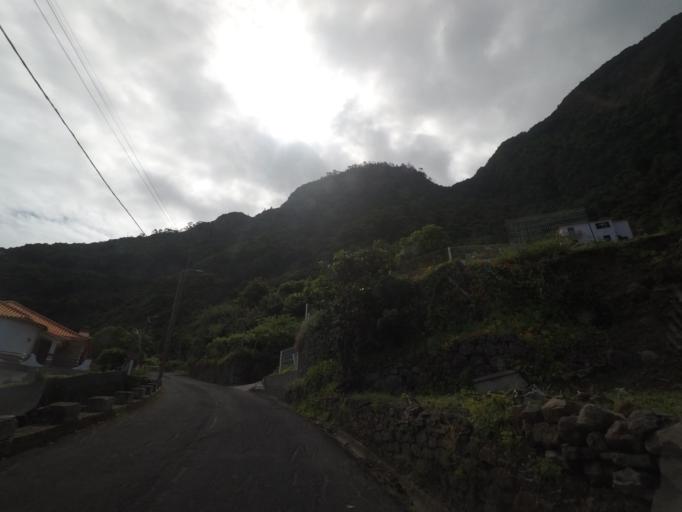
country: PT
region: Madeira
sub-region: Sao Vicente
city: Sao Vicente
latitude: 32.8202
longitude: -16.9908
